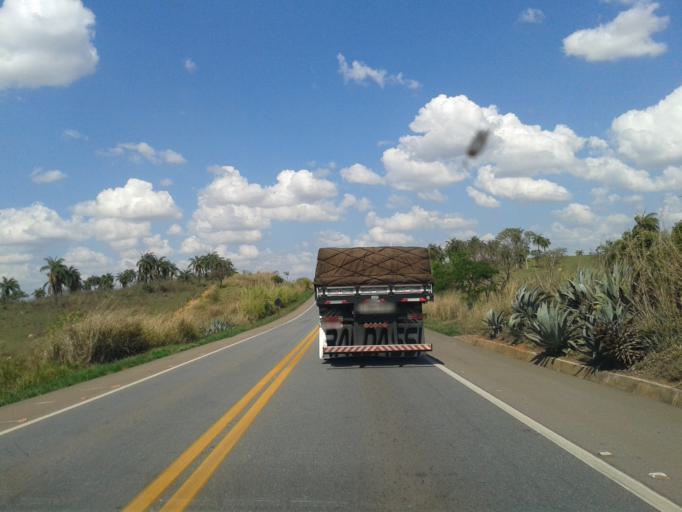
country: BR
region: Minas Gerais
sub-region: Luz
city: Luz
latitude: -19.7423
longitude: -45.8413
